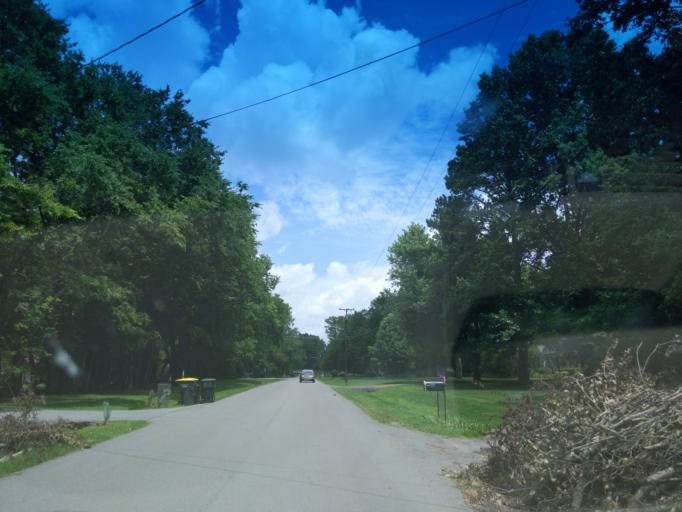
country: US
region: Tennessee
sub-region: Williamson County
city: Brentwood Estates
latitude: 36.0144
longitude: -86.7759
